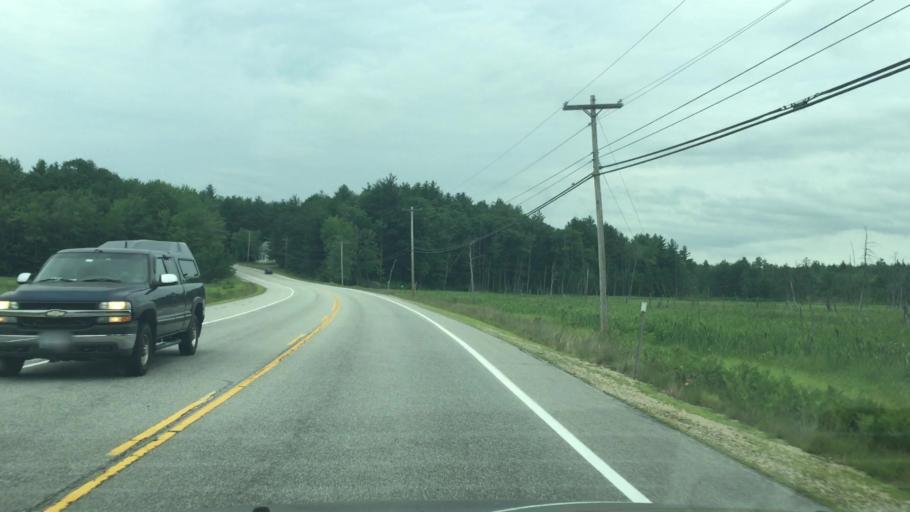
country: US
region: New Hampshire
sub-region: Carroll County
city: Sandwich
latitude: 43.8066
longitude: -71.3547
